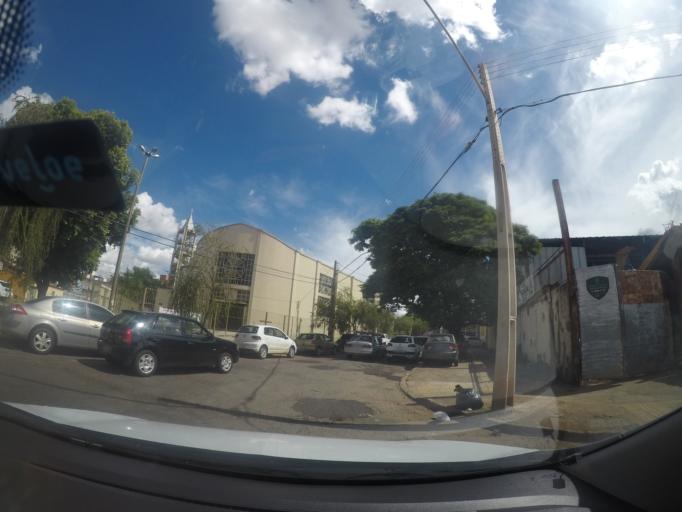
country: BR
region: Goias
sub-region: Goiania
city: Goiania
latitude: -16.6704
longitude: -49.3069
